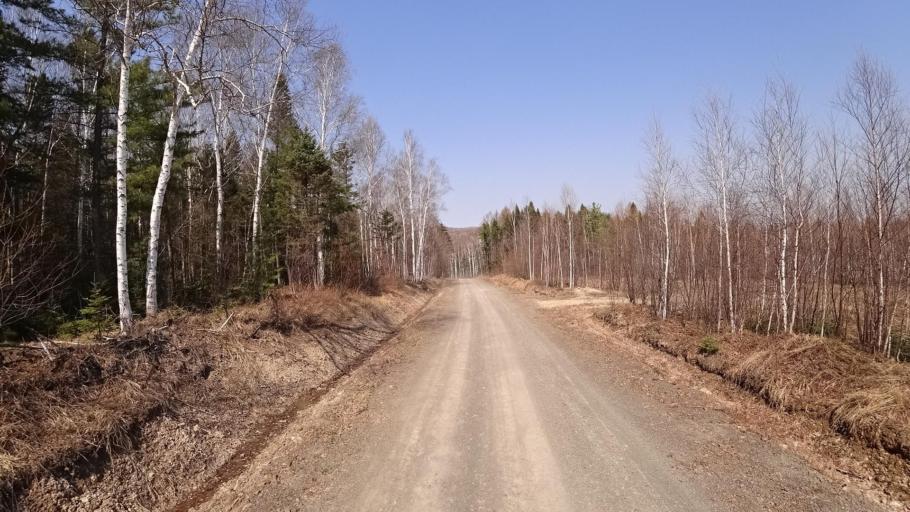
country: RU
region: Khabarovsk Krai
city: Selikhino
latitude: 50.6323
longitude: 137.4072
